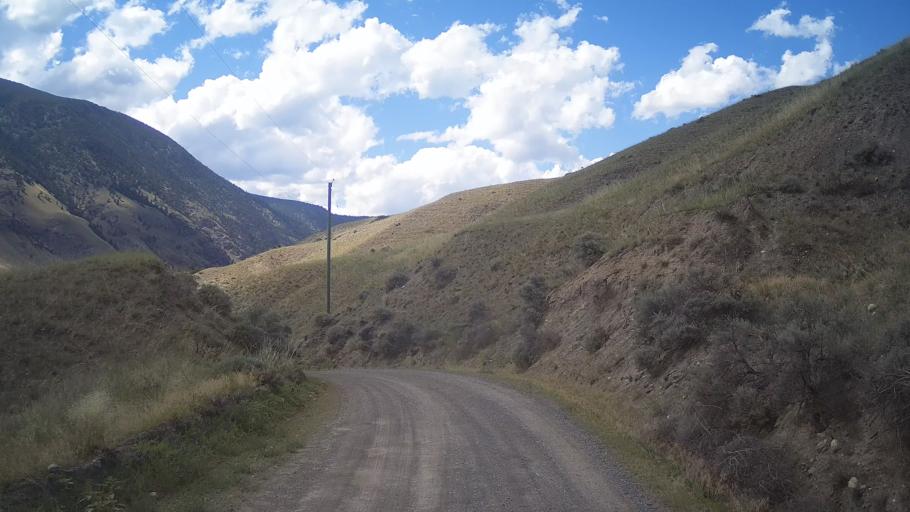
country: CA
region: British Columbia
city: Lillooet
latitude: 51.1815
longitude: -122.1207
